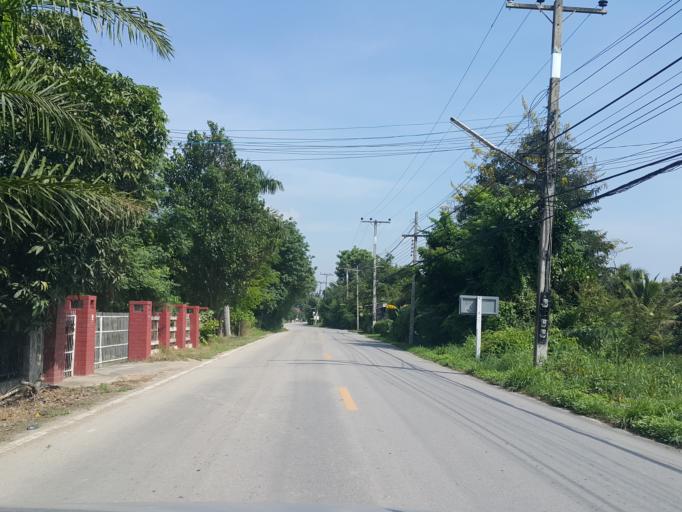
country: TH
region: Chiang Mai
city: Saraphi
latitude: 18.6843
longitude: 99.0615
